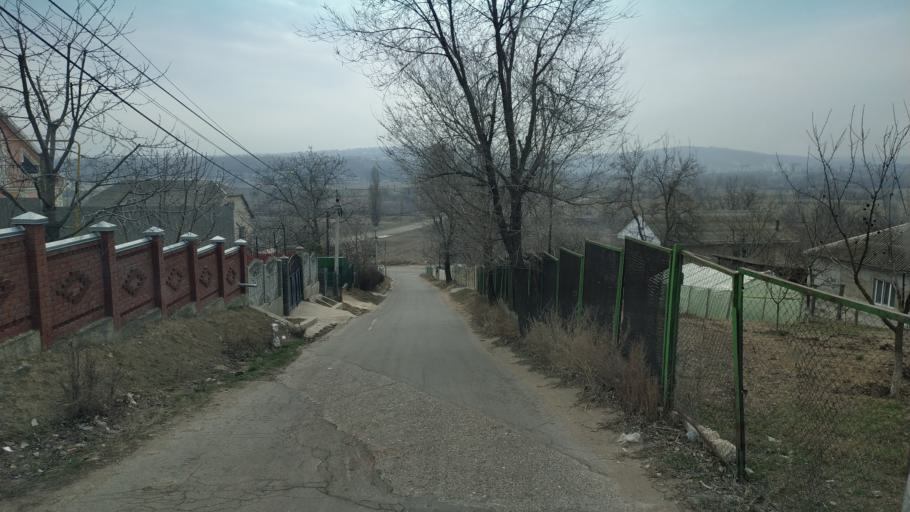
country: MD
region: Chisinau
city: Singera
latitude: 46.9339
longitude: 28.9848
